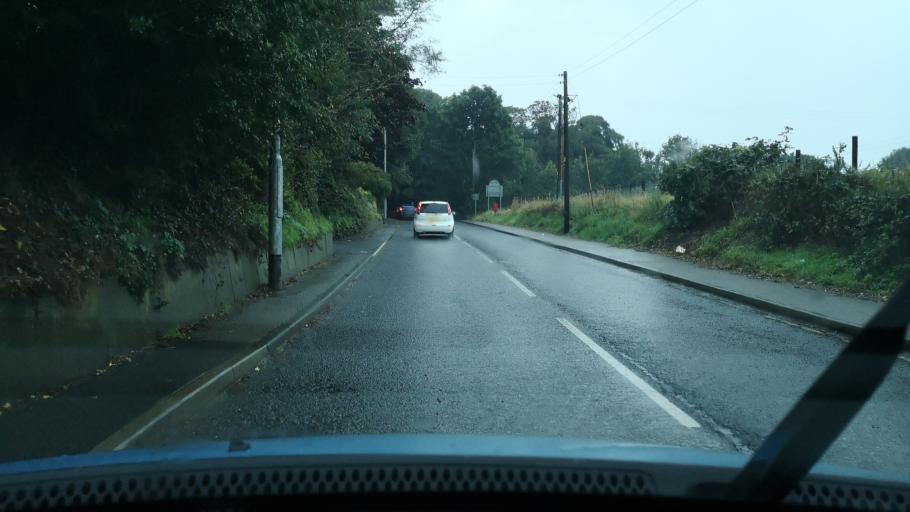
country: GB
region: England
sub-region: City and Borough of Wakefield
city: Sharlston
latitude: 53.6594
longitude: -1.4124
